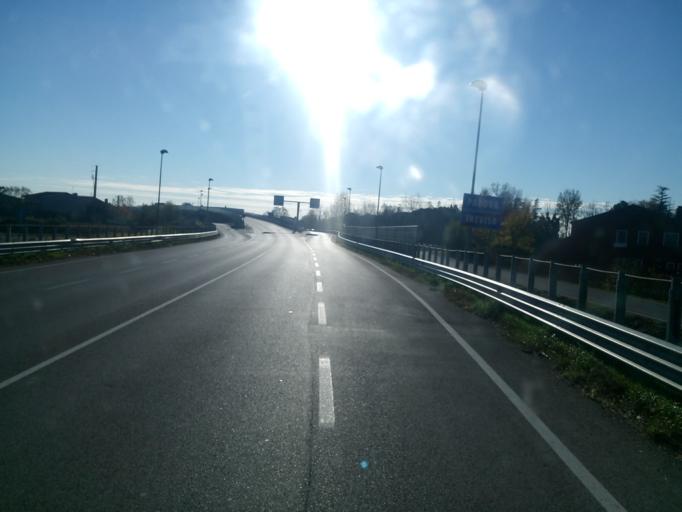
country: IT
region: Veneto
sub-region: Provincia di Padova
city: Loreggia
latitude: 45.6172
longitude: 11.9434
